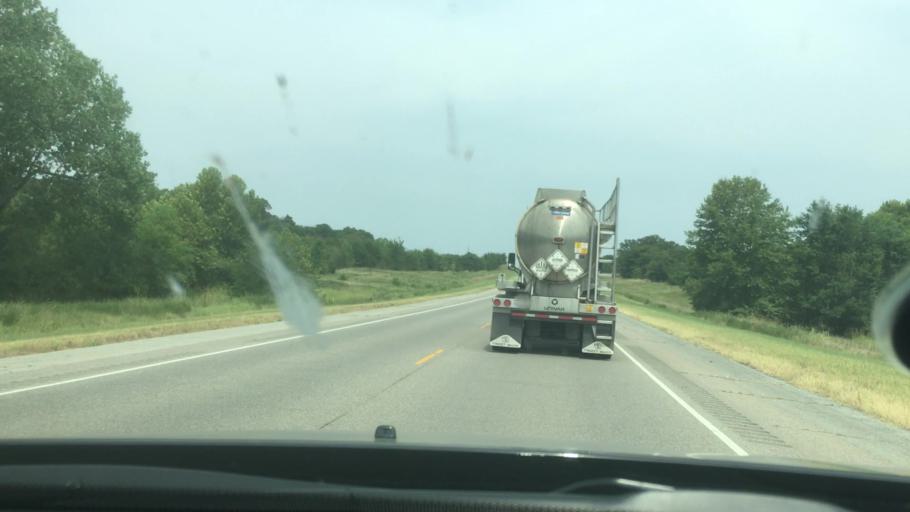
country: US
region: Oklahoma
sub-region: Pontotoc County
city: Ada
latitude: 34.6303
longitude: -96.4688
